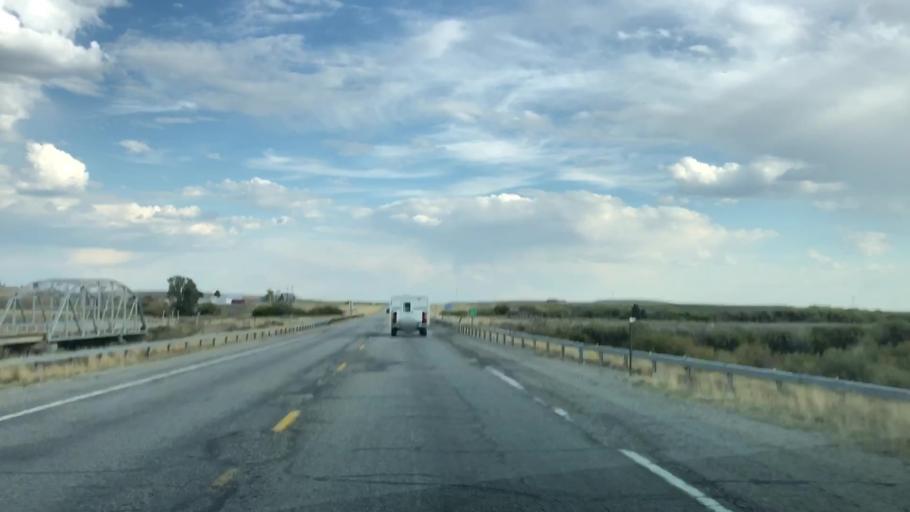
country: US
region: Wyoming
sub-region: Sublette County
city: Pinedale
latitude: 43.0196
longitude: -110.1200
